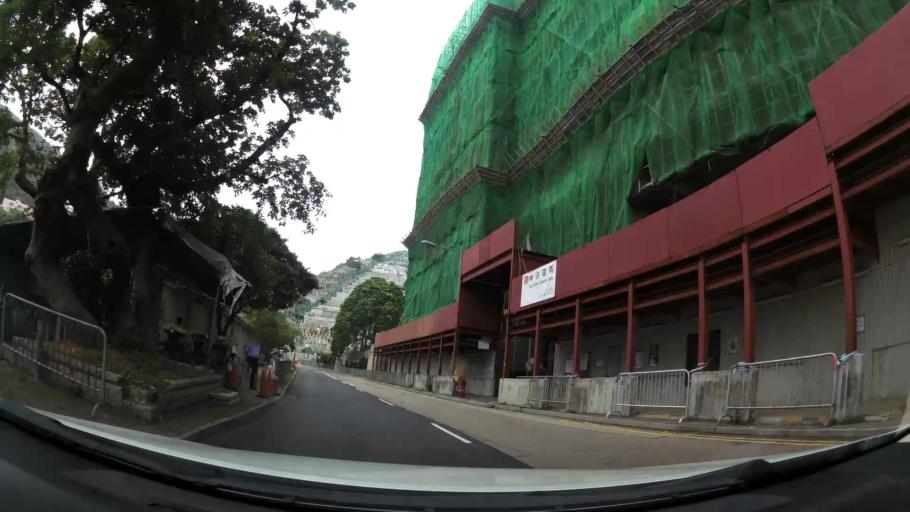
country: HK
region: Central and Western
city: Central
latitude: 22.2717
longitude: 114.1274
